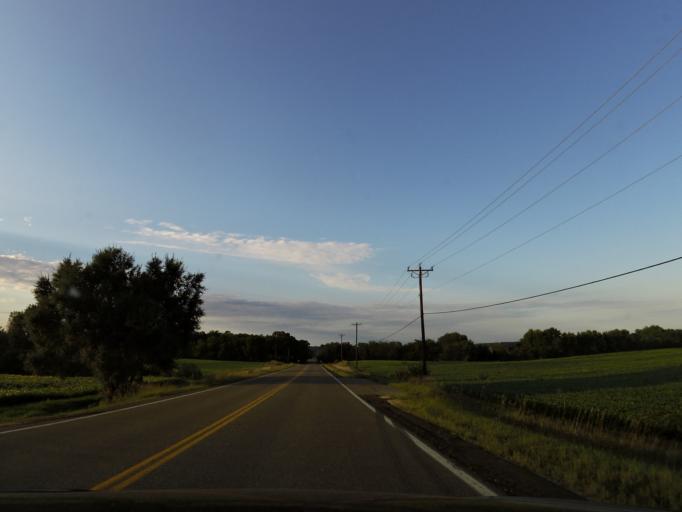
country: US
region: Minnesota
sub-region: Washington County
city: Afton
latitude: 44.9245
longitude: -92.8428
